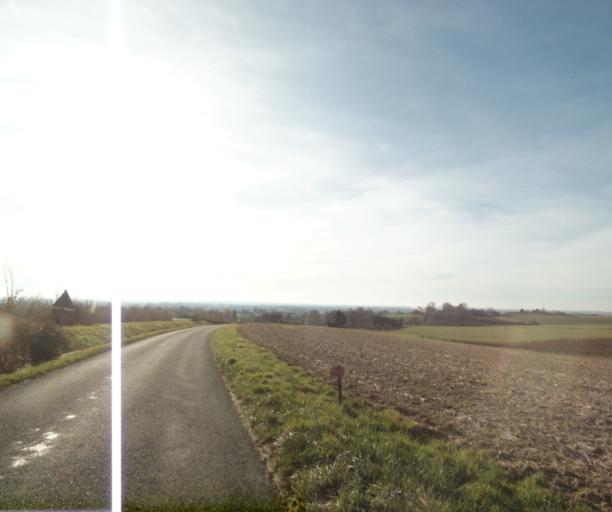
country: FR
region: Poitou-Charentes
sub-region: Departement de la Charente-Maritime
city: Chaniers
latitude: 45.7256
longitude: -0.5527
